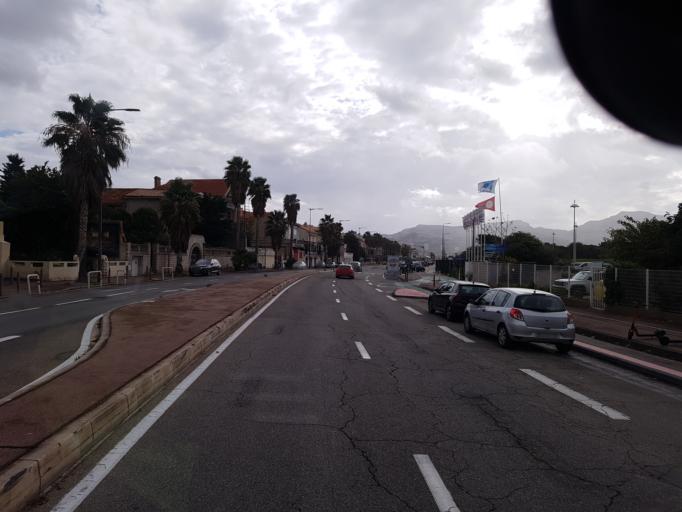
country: FR
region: Provence-Alpes-Cote d'Azur
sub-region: Departement des Bouches-du-Rhone
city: Marseille 08
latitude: 43.2675
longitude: 5.3720
